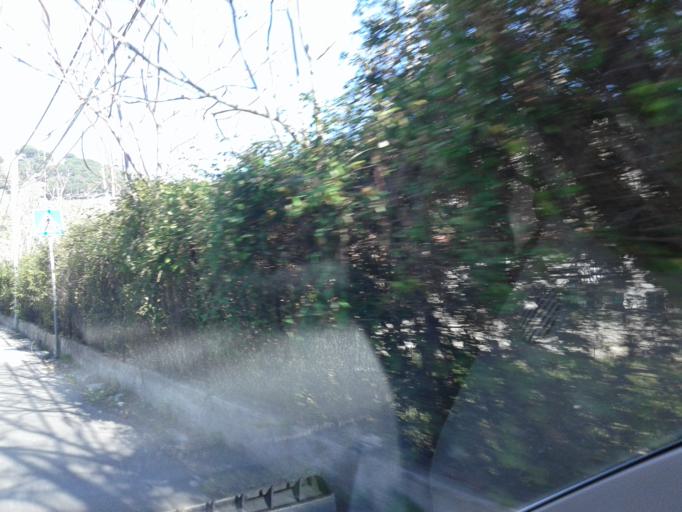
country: IT
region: Sicily
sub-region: Palermo
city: Piano dei Geli
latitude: 38.1158
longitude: 13.2899
